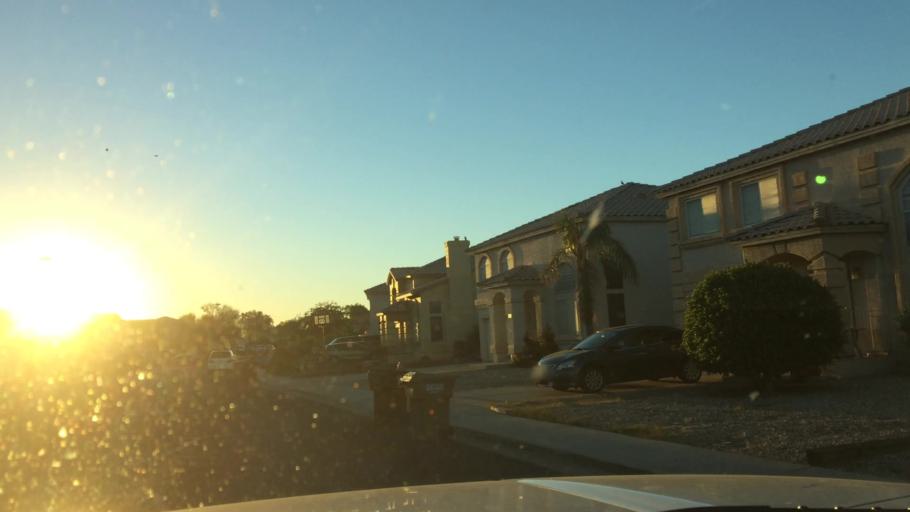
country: US
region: Arizona
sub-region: Maricopa County
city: Sun City
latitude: 33.5690
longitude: -112.2673
